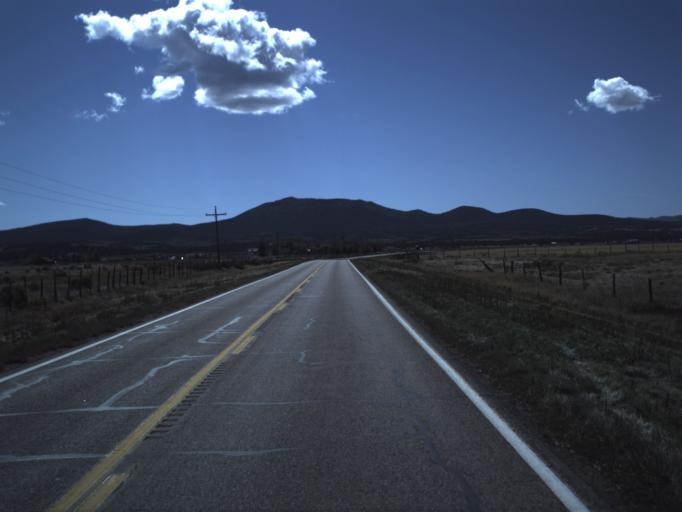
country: US
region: Utah
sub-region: Washington County
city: Enterprise
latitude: 37.6045
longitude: -113.6612
